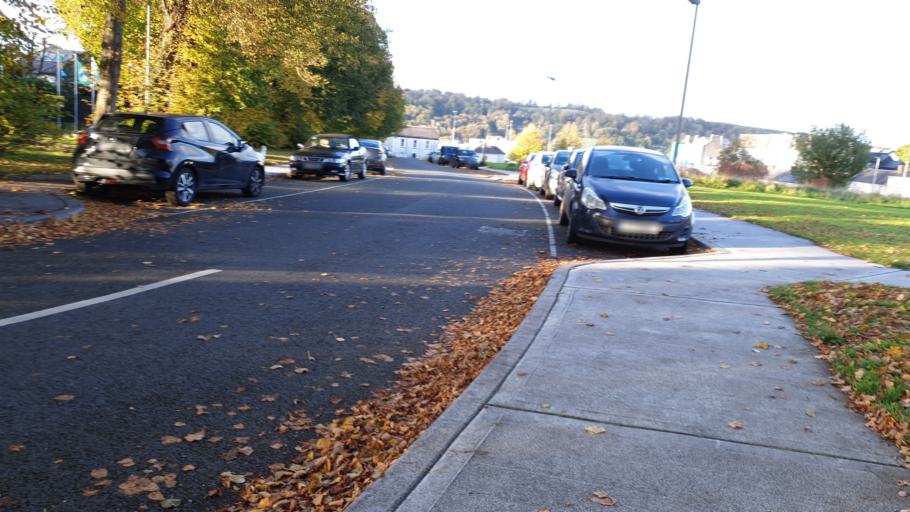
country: IE
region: Munster
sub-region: County Cork
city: Cork
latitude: 51.8956
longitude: -8.4133
